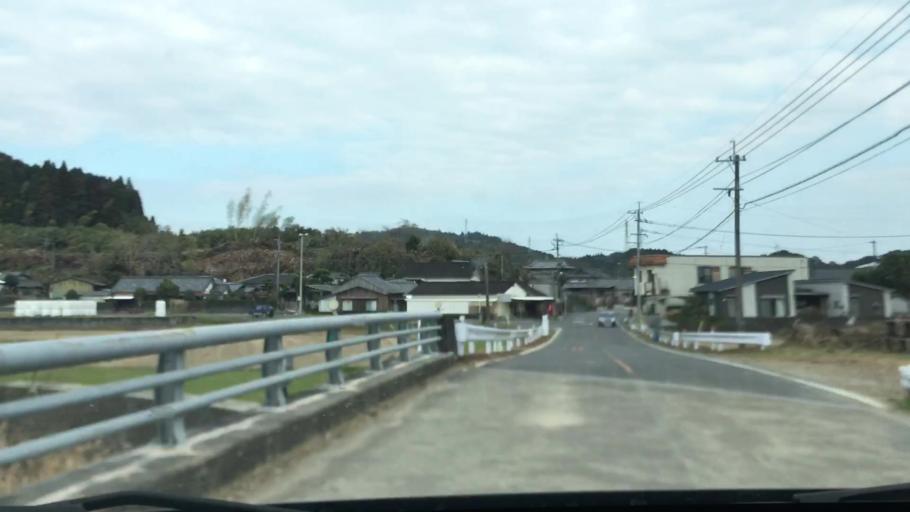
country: JP
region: Miyazaki
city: Kushima
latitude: 31.4673
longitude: 131.2084
